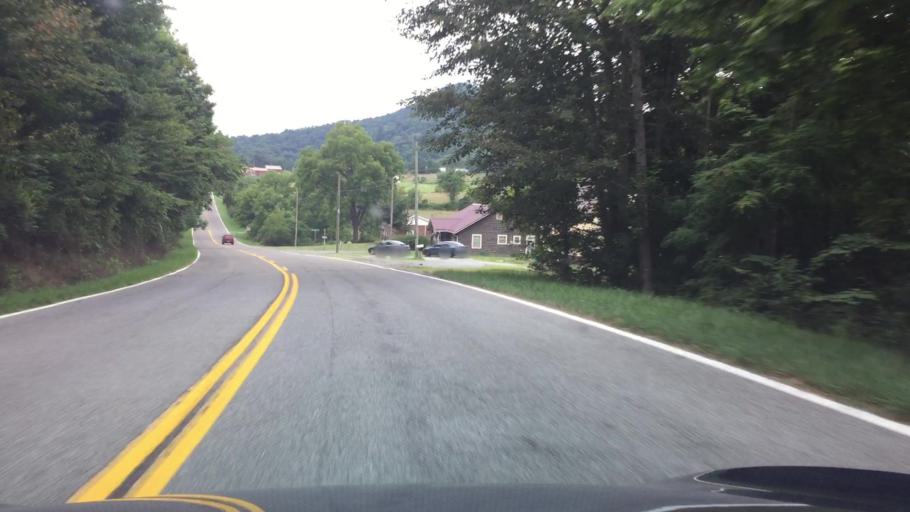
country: US
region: Virginia
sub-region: Pulaski County
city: Pulaski
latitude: 36.9774
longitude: -80.8392
